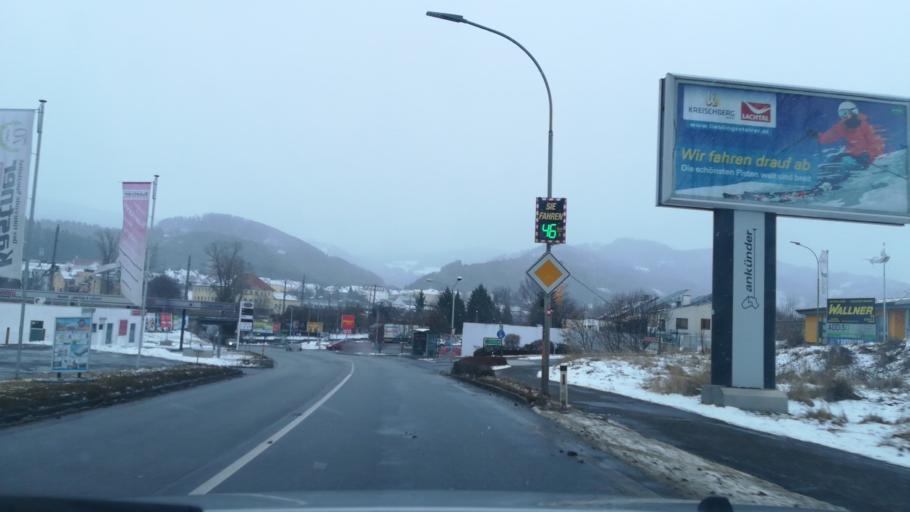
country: AT
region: Styria
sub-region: Politischer Bezirk Murtal
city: Judenburg
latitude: 47.1775
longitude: 14.6668
